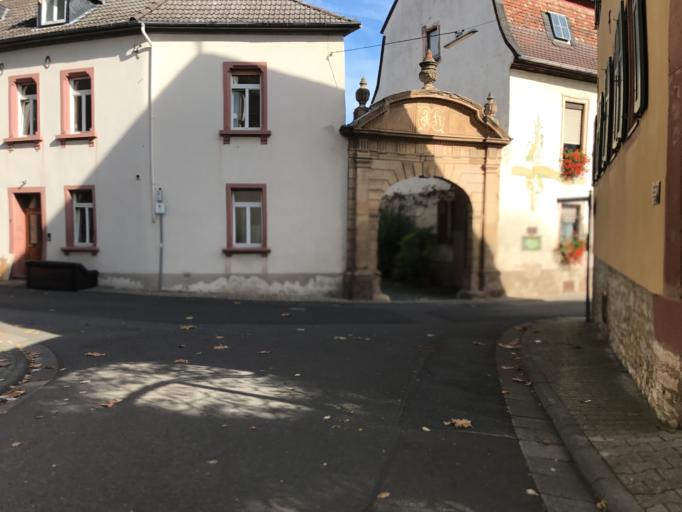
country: DE
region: Rheinland-Pfalz
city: Gau-Algesheim
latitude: 49.9560
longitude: 8.0171
